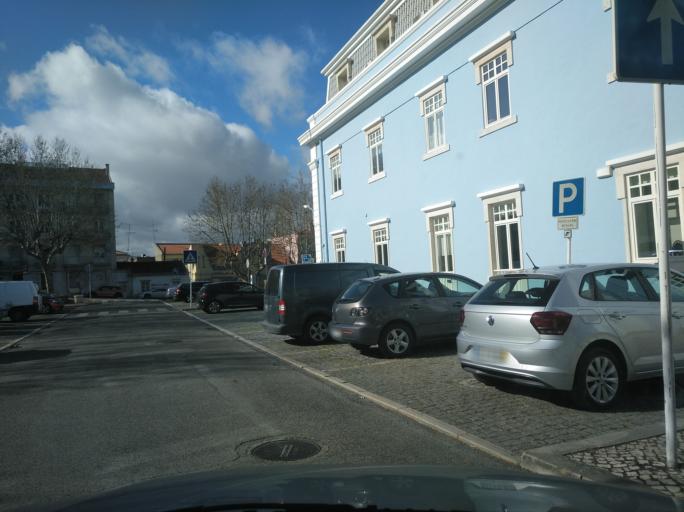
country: PT
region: Lisbon
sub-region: Loures
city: Loures
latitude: 38.8304
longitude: -9.1687
